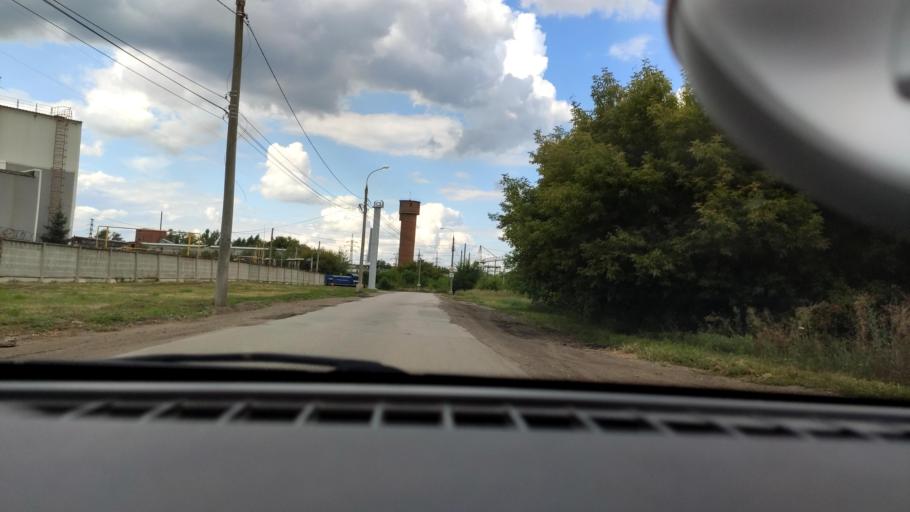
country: RU
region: Samara
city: Novokuybyshevsk
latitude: 53.1075
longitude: 50.0418
